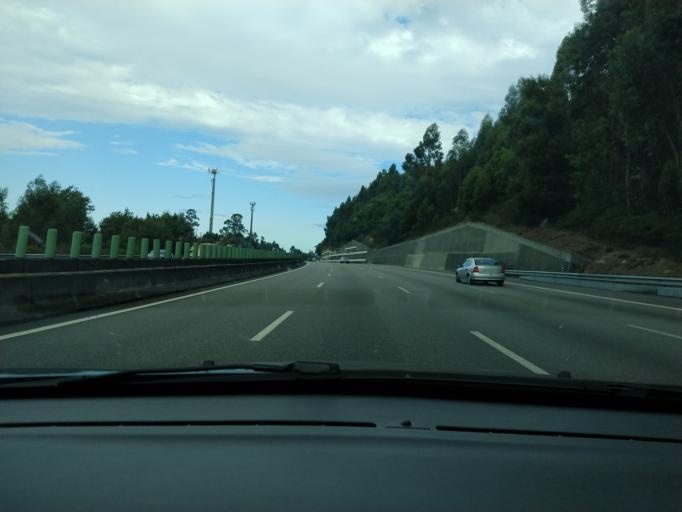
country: PT
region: Porto
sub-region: Vila Nova de Gaia
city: Perozinho
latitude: 41.0518
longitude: -8.5730
